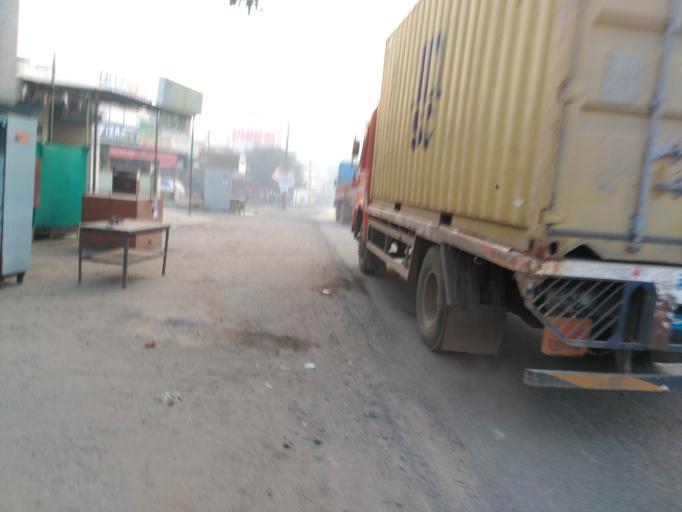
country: IN
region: Maharashtra
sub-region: Pune Division
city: Pune
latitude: 18.4493
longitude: 73.9063
